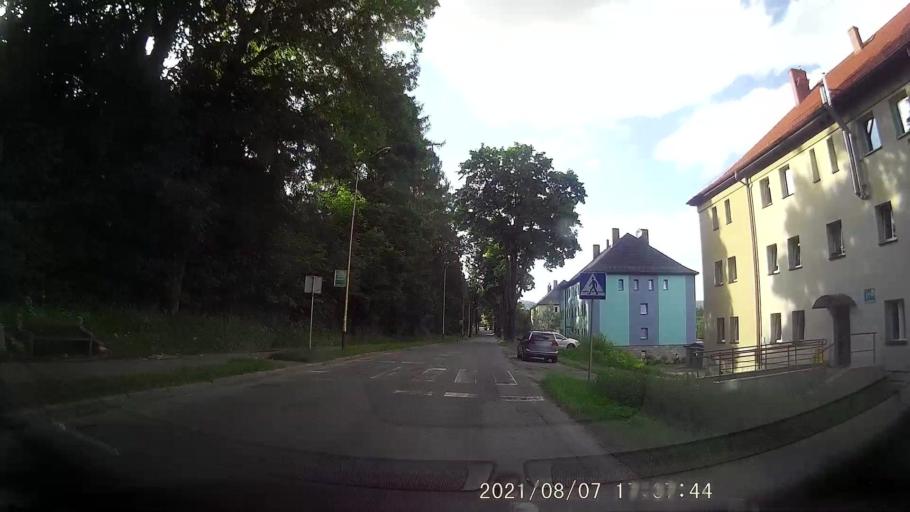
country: PL
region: Lower Silesian Voivodeship
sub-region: Powiat klodzki
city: Szczytna
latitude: 50.4059
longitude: 16.4530
